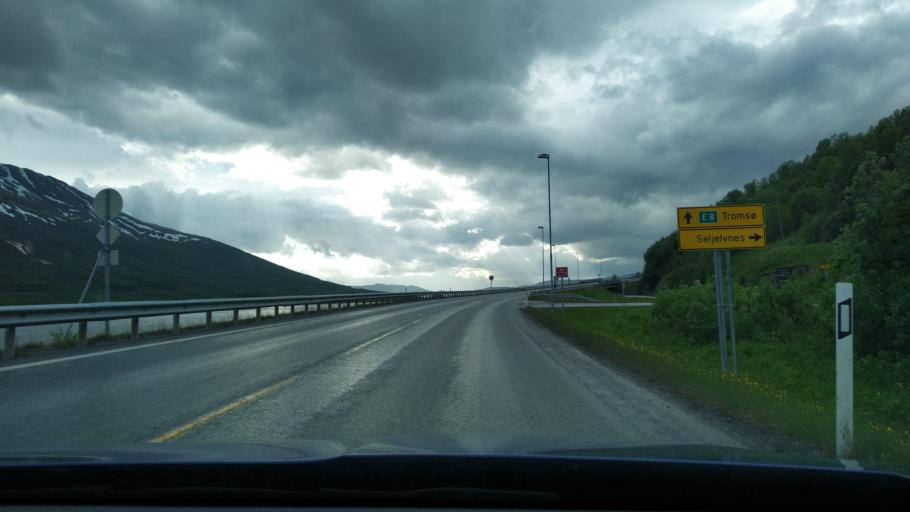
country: NO
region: Troms
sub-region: Balsfjord
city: Storsteinnes
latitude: 69.2224
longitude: 19.5149
